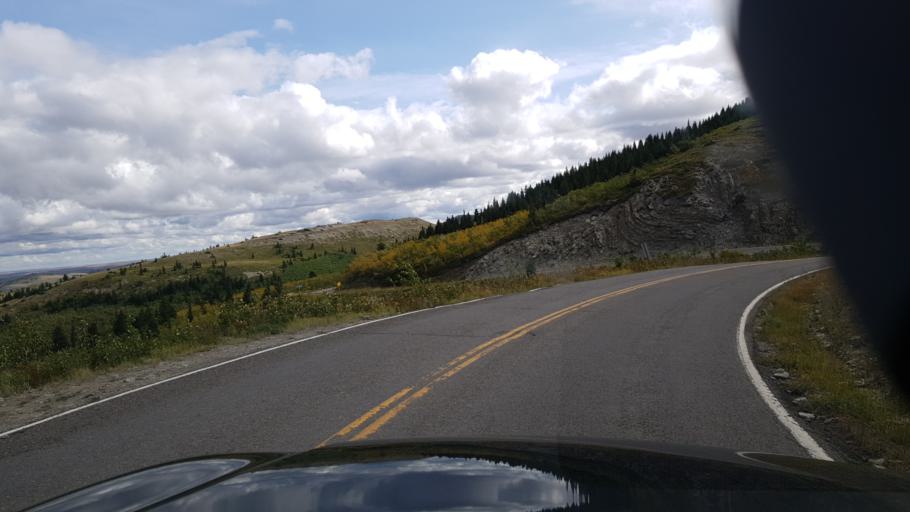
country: US
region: Montana
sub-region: Glacier County
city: South Browning
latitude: 48.5457
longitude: -113.2902
